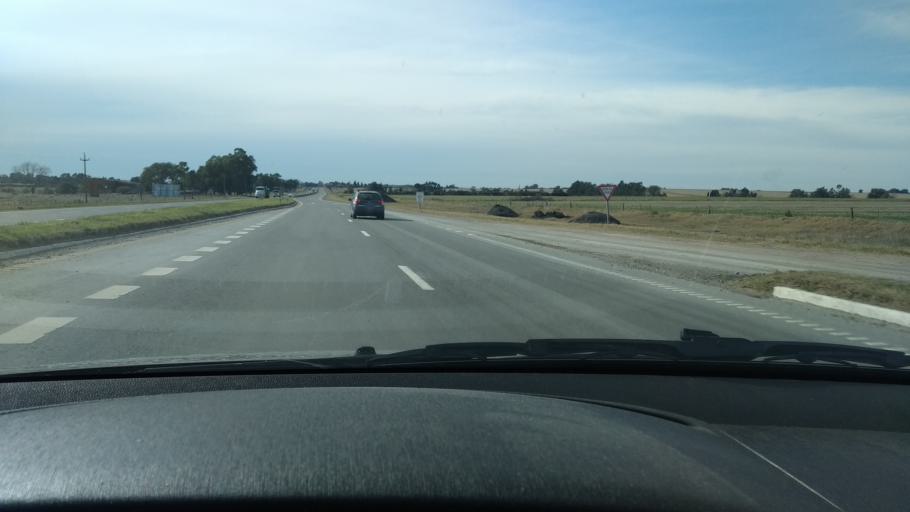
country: AR
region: Buenos Aires
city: Olavarria
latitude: -36.8891
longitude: -60.1576
